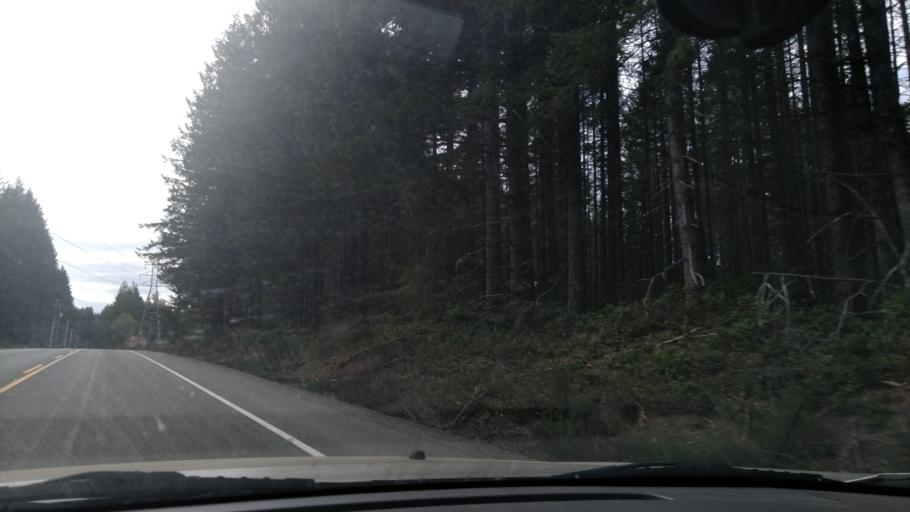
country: CA
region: British Columbia
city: Campbell River
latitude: 50.0308
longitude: -125.3425
